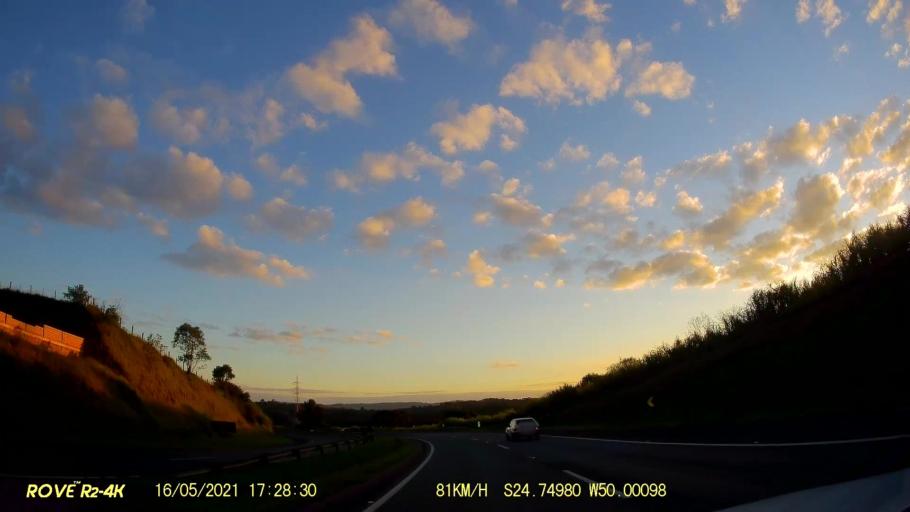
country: BR
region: Parana
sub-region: Castro
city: Castro
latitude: -24.7505
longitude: -50.0010
